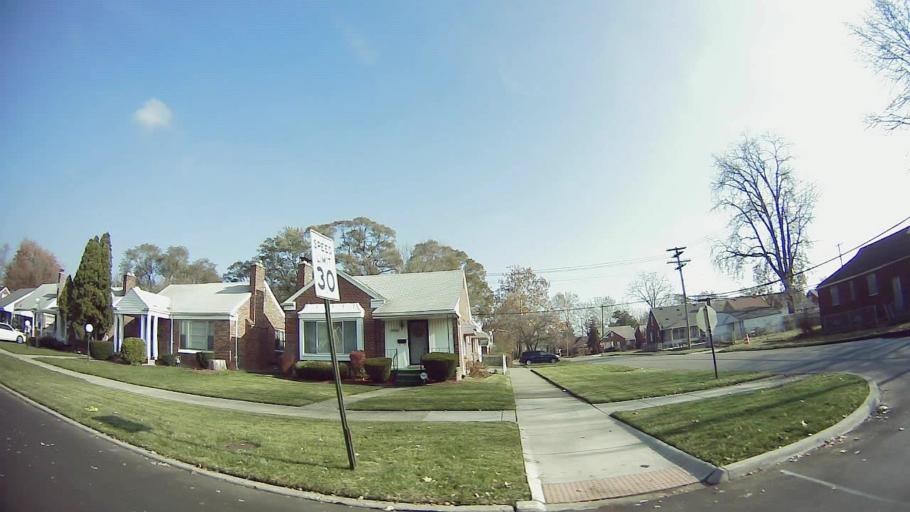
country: US
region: Michigan
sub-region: Oakland County
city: Oak Park
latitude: 42.4372
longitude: -83.1904
